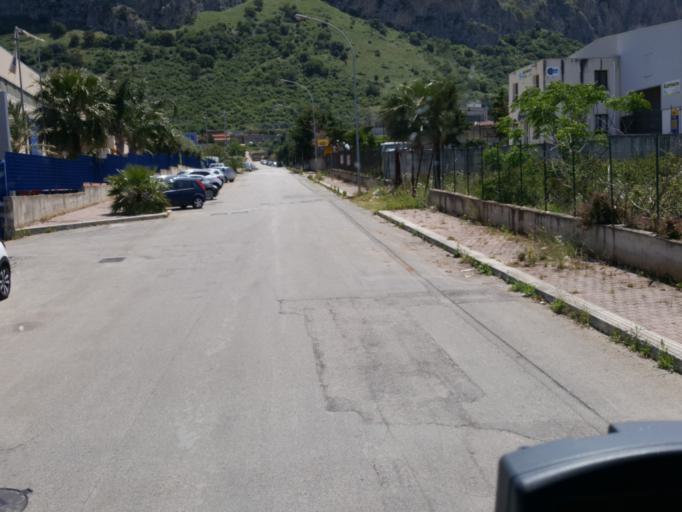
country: IT
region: Sicily
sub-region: Palermo
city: Carini
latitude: 38.1563
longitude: 13.2100
